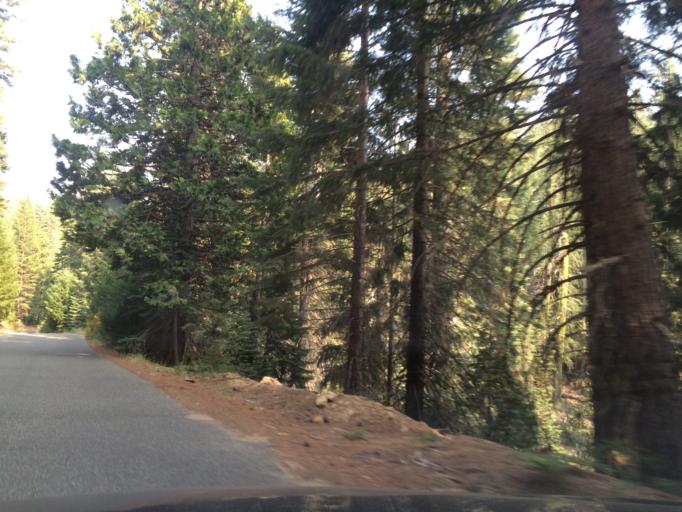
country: US
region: California
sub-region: Sierra County
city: Downieville
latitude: 39.3789
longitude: -120.6726
